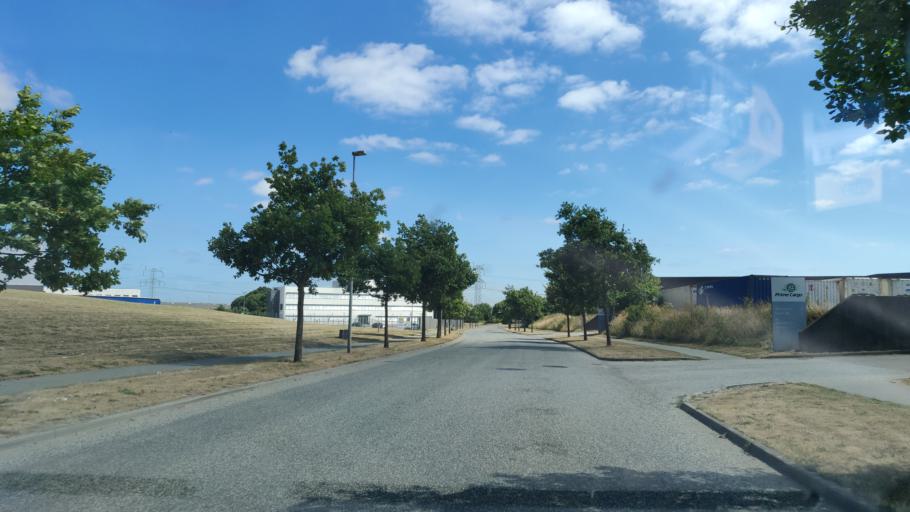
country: DK
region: South Denmark
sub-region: Kolding Kommune
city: Kolding
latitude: 55.5406
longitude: 9.4951
